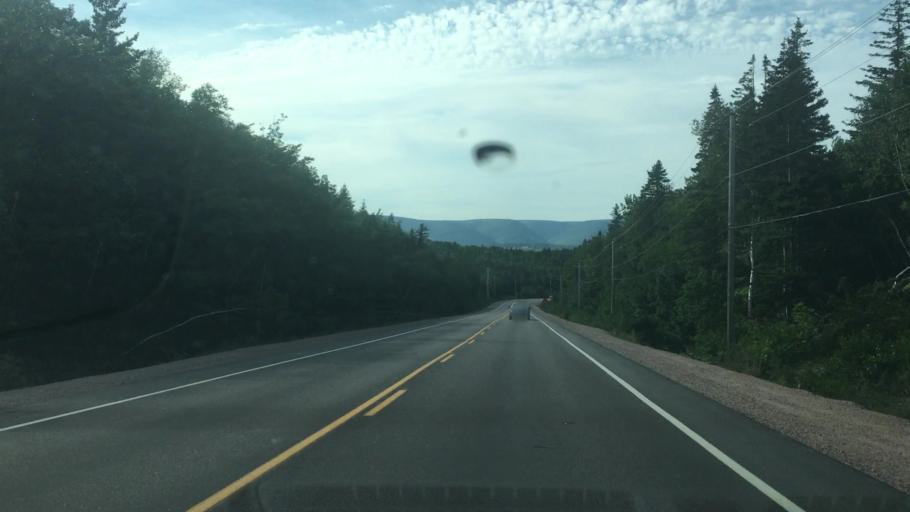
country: CA
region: Nova Scotia
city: Sydney Mines
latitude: 46.8562
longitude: -60.4588
